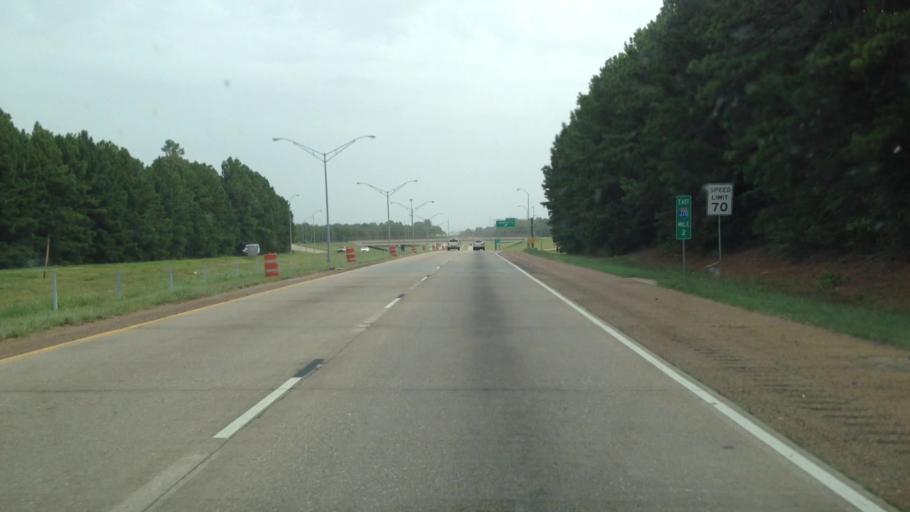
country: US
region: Louisiana
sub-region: Caddo Parish
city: Shreveport
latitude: 32.4812
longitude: -93.8313
